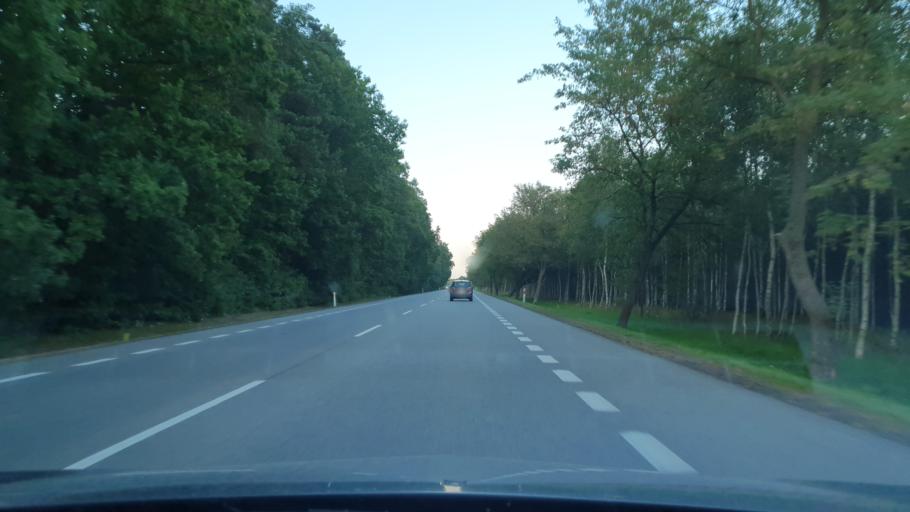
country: PL
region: Pomeranian Voivodeship
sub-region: Powiat leborski
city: Nowa Wies Leborska
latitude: 54.4957
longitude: 17.6170
